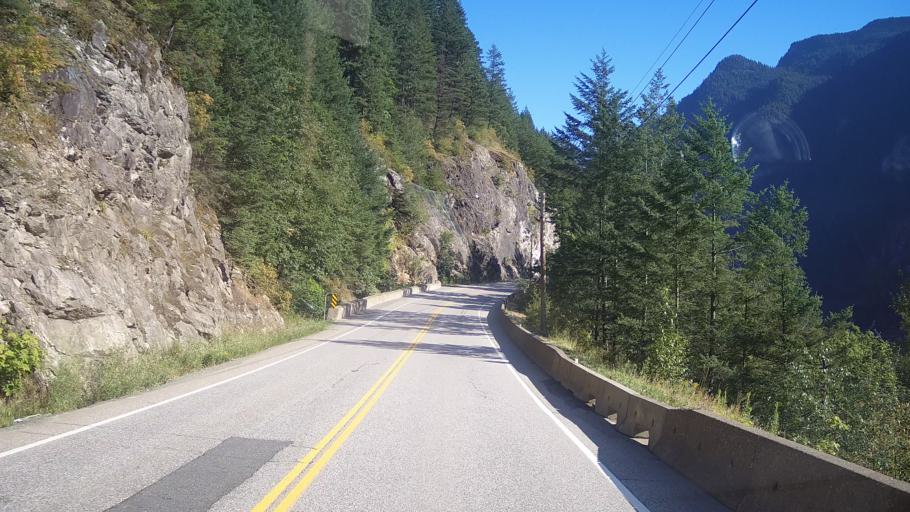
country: CA
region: British Columbia
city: Hope
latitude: 49.5711
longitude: -121.4036
